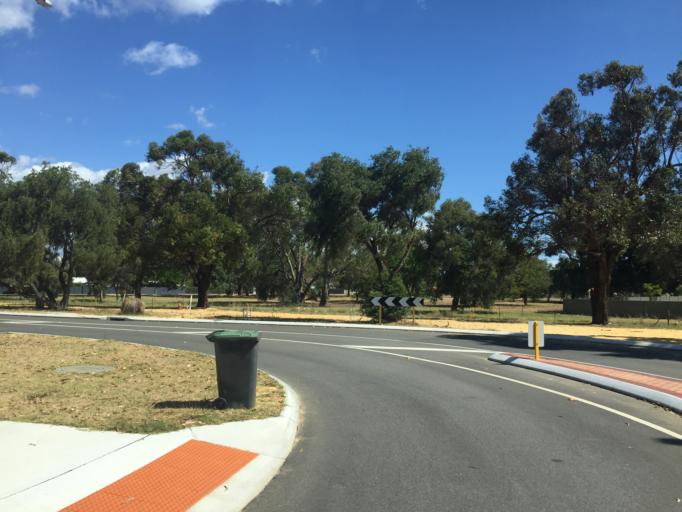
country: AU
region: Western Australia
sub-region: Belmont
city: Redcliffe
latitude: -31.9322
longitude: 115.9442
